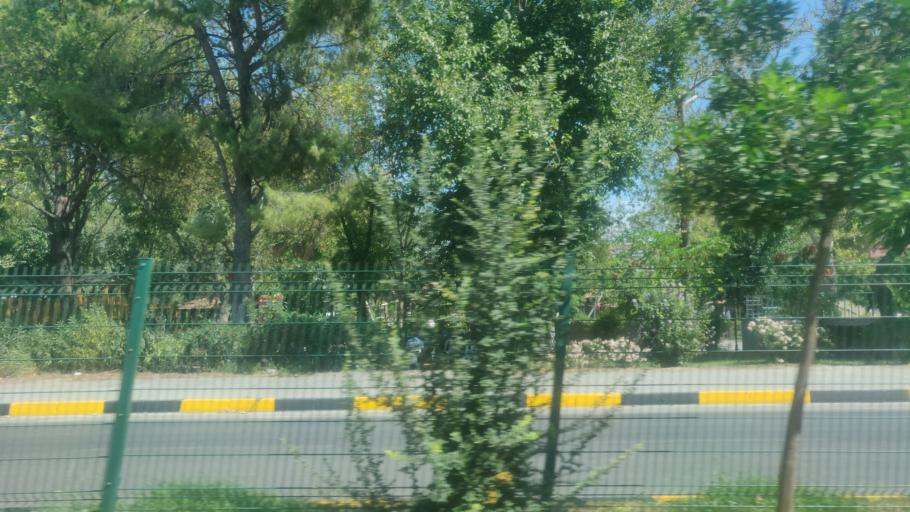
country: TR
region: Mugla
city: Dalaman
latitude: 36.7679
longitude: 28.7998
